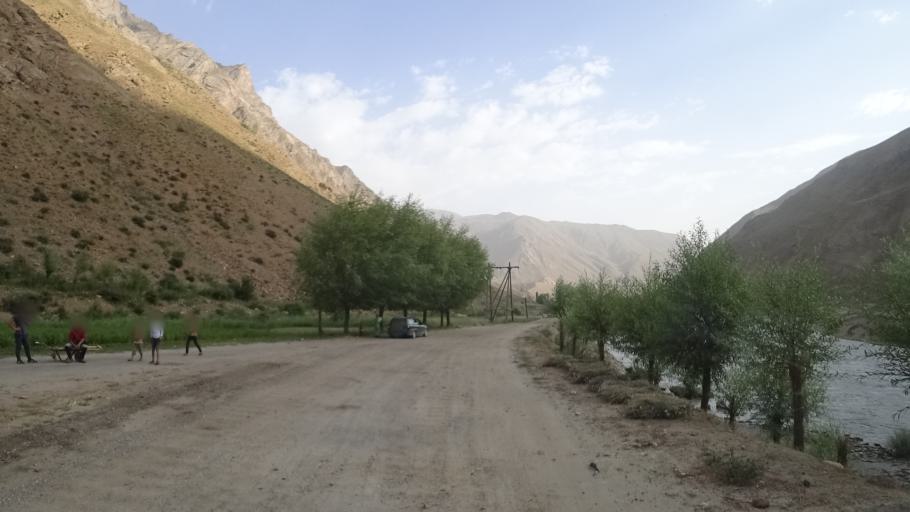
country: TJ
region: Gorno-Badakhshan
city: Khorugh
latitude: 37.2570
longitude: 71.4860
